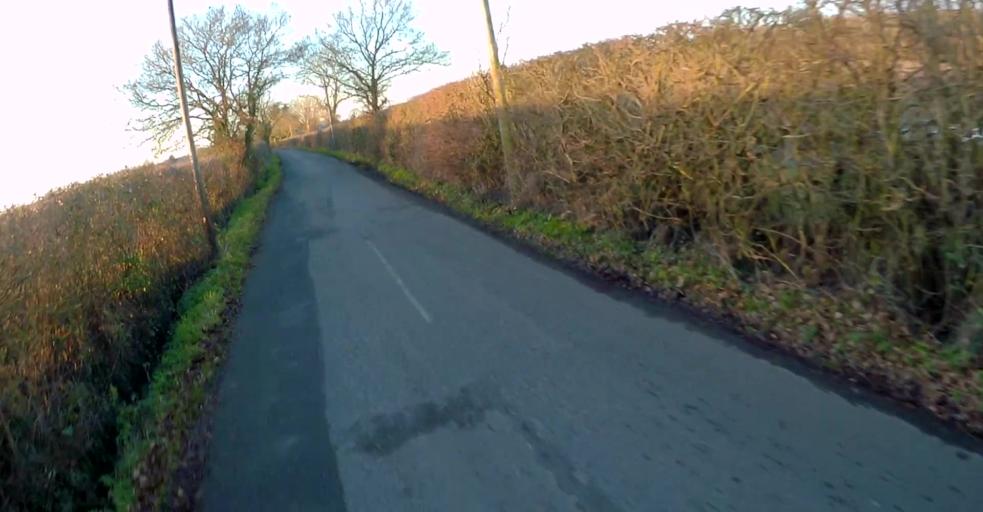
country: GB
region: England
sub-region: West Berkshire
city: Stratfield Mortimer
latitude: 51.3467
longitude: -1.0106
